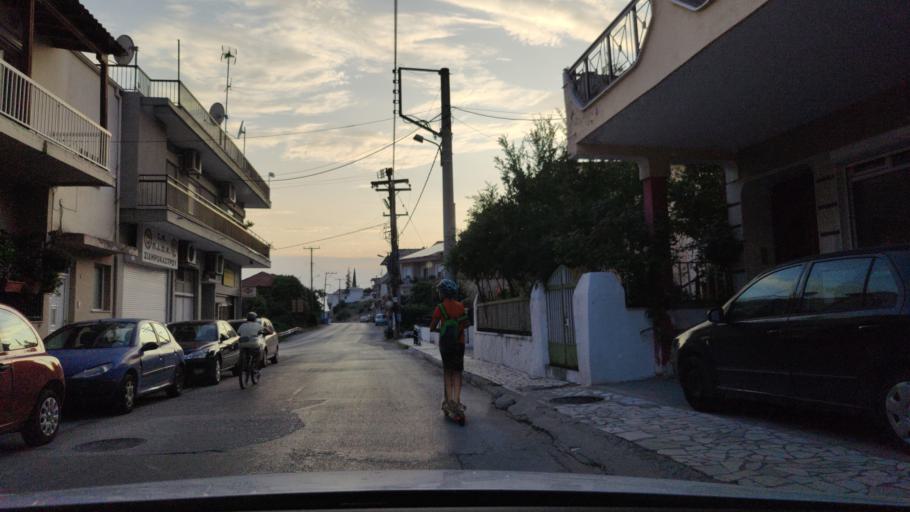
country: GR
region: Central Macedonia
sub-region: Nomos Serron
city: Sidirokastro
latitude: 41.2403
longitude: 23.3918
